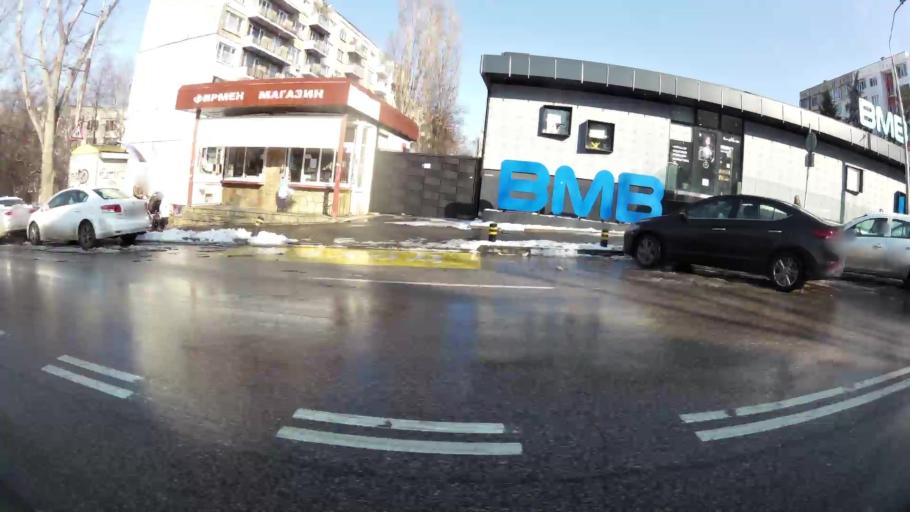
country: BG
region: Sofia-Capital
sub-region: Stolichna Obshtina
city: Sofia
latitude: 42.6616
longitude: 23.3462
